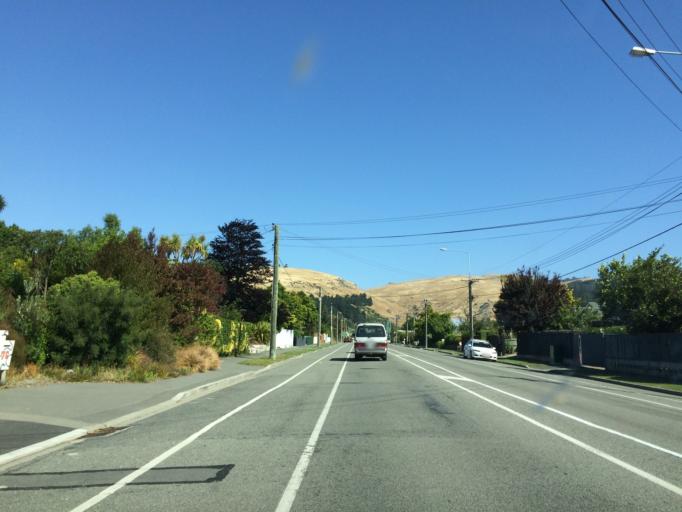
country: NZ
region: Canterbury
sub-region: Christchurch City
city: Christchurch
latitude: -43.5597
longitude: 172.6552
